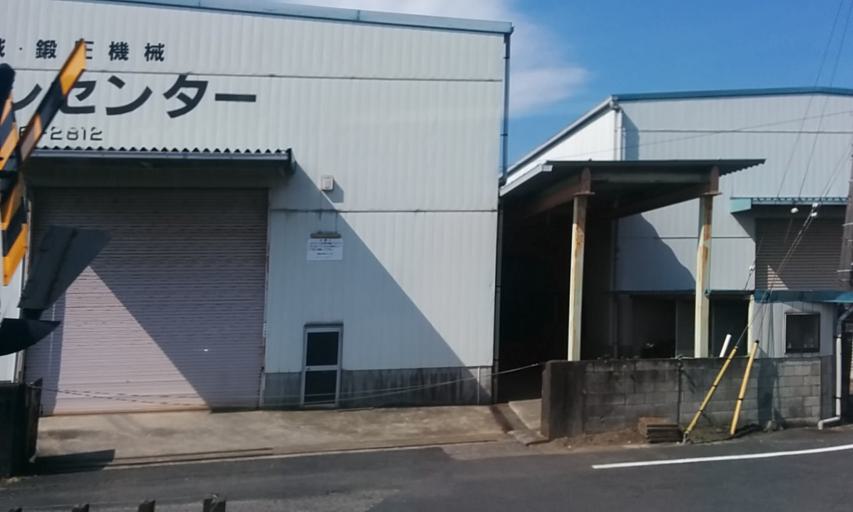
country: JP
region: Saitama
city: Kazo
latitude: 36.1346
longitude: 139.5785
